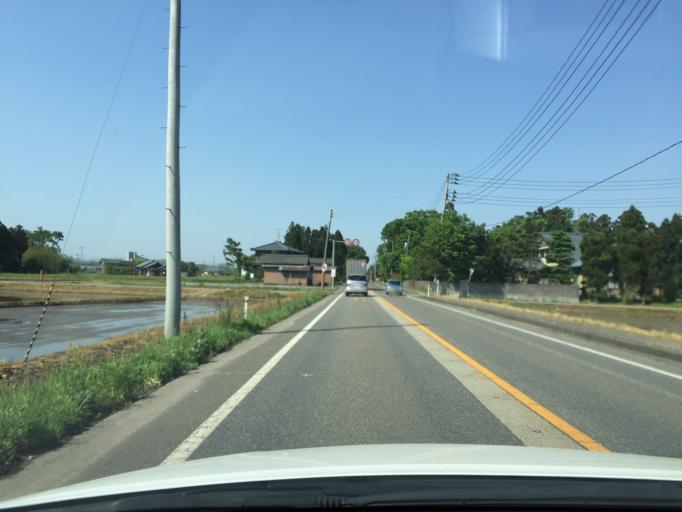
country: JP
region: Niigata
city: Muramatsu
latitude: 37.7156
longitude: 139.2164
